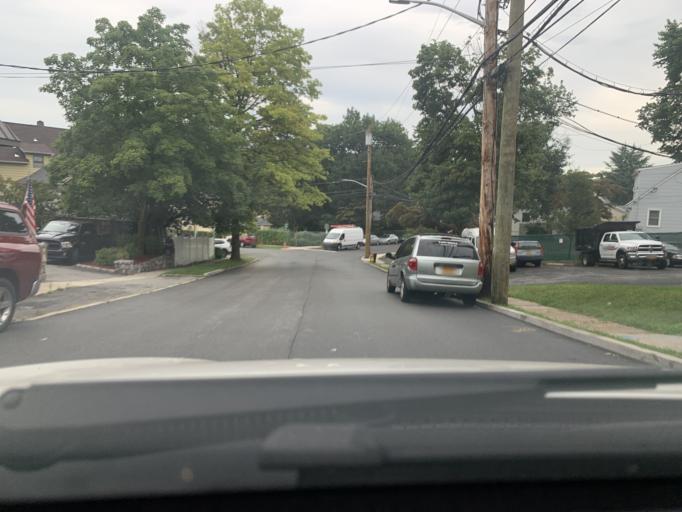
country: US
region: New York
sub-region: Westchester County
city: Ossining
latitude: 41.1666
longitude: -73.8555
